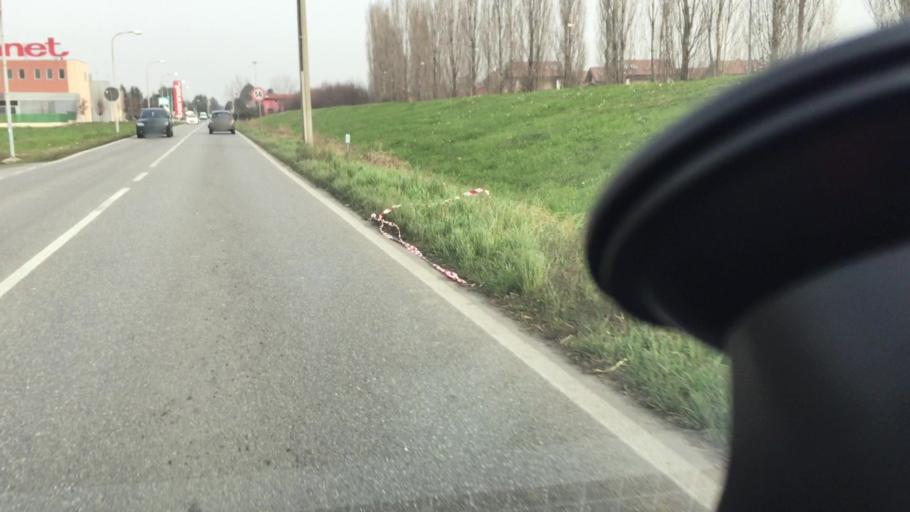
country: IT
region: Lombardy
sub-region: Citta metropolitana di Milano
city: Vaprio d'Adda
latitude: 45.5691
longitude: 9.5198
